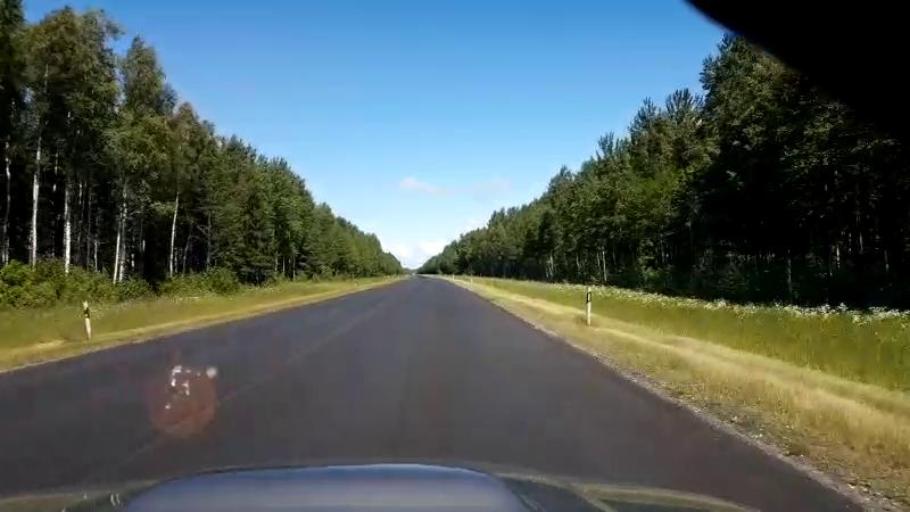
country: LV
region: Salacgrivas
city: Ainazi
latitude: 57.9162
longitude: 24.4210
